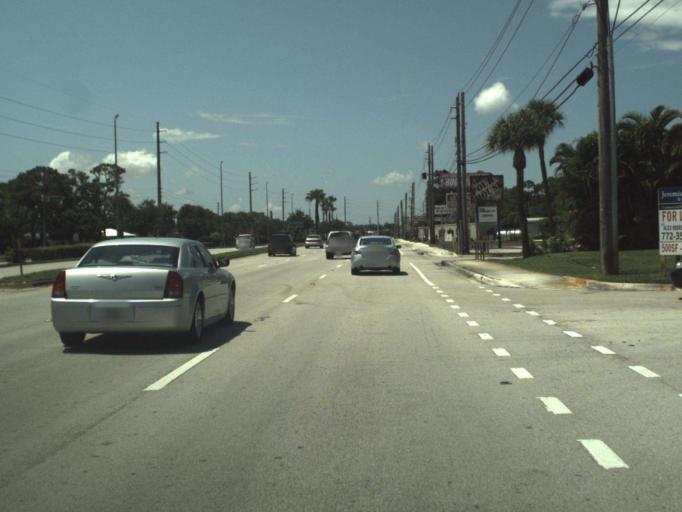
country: US
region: Florida
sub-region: Saint Lucie County
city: River Park
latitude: 27.3303
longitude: -80.3228
